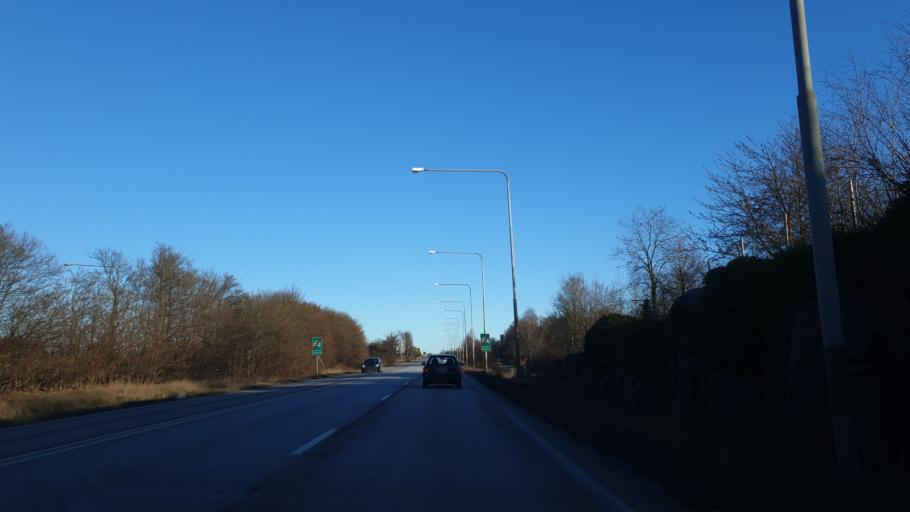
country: SE
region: Blekinge
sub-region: Karlskrona Kommun
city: Karlskrona
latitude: 56.1900
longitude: 15.6219
